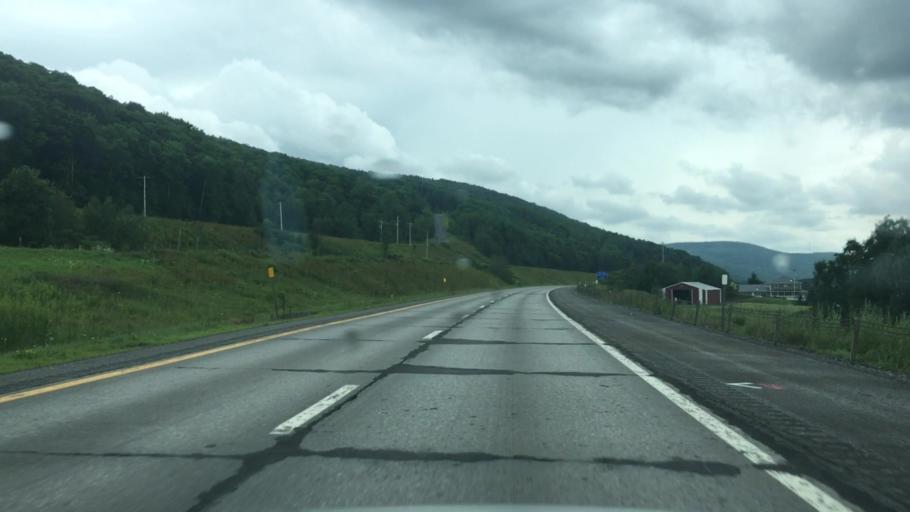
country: US
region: New York
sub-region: Otsego County
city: Worcester
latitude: 42.6221
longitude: -74.6645
